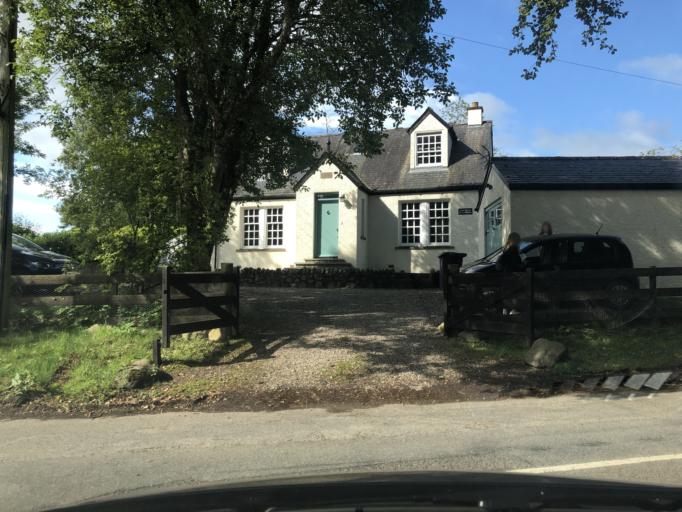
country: GB
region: Scotland
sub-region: Angus
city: Kirriemuir
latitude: 56.7301
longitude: -3.0045
